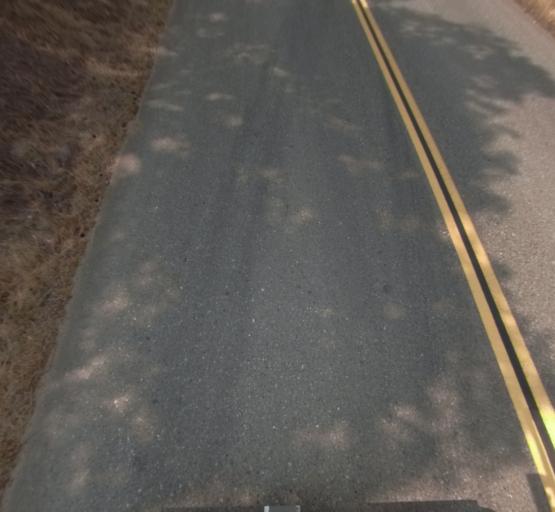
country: US
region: California
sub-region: Madera County
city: Yosemite Lakes
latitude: 37.1711
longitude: -119.8343
